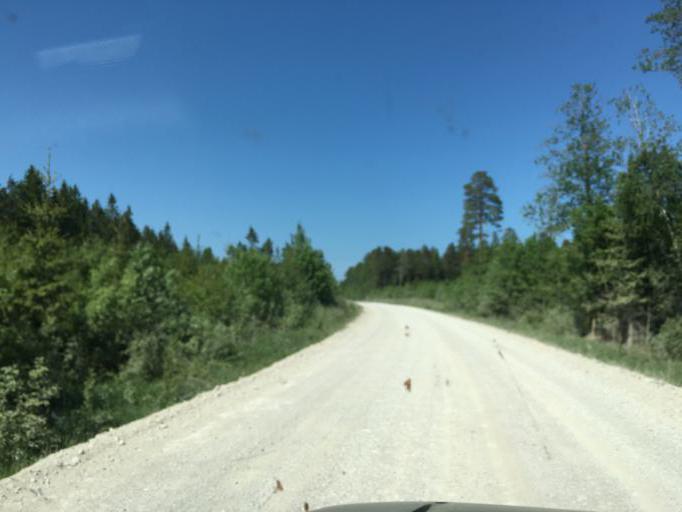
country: LV
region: Dundaga
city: Dundaga
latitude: 57.4374
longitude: 22.3174
